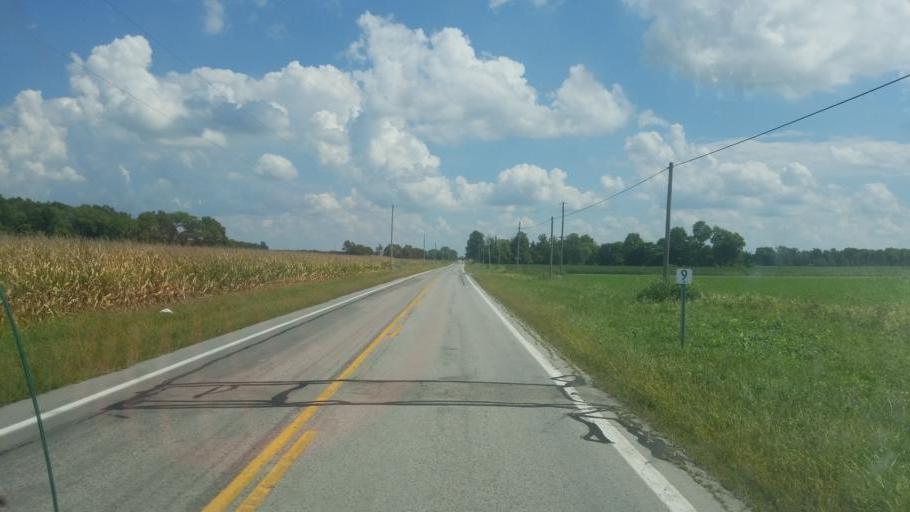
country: US
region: Ohio
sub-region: Hancock County
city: Arlington
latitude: 40.8924
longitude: -83.7093
